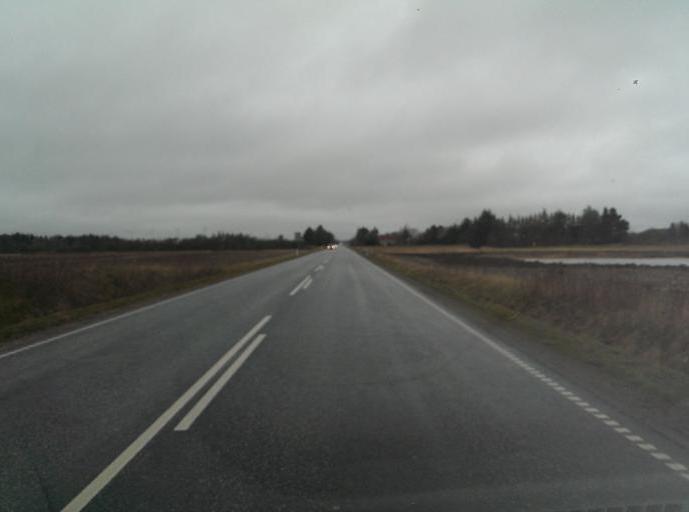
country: DK
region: Central Jutland
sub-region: Ringkobing-Skjern Kommune
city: Ringkobing
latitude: 56.1474
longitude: 8.2831
